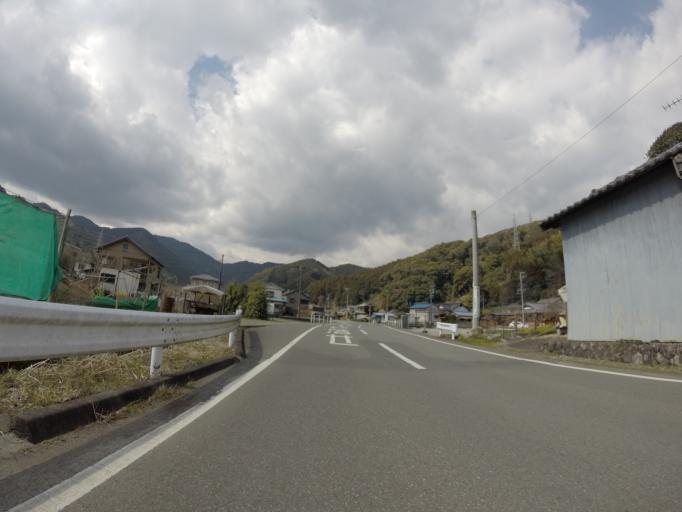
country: JP
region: Shizuoka
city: Shizuoka-shi
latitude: 35.0522
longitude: 138.3529
